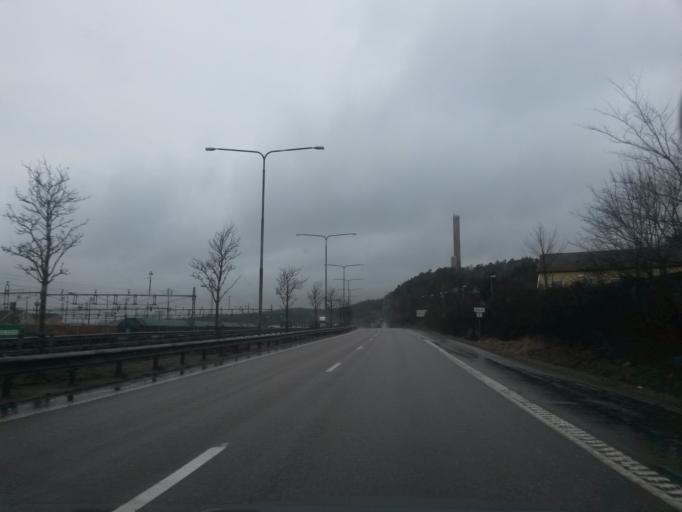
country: SE
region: Vaestra Goetaland
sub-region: Uddevalla Kommun
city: Uddevalla
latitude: 58.3546
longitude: 11.9256
